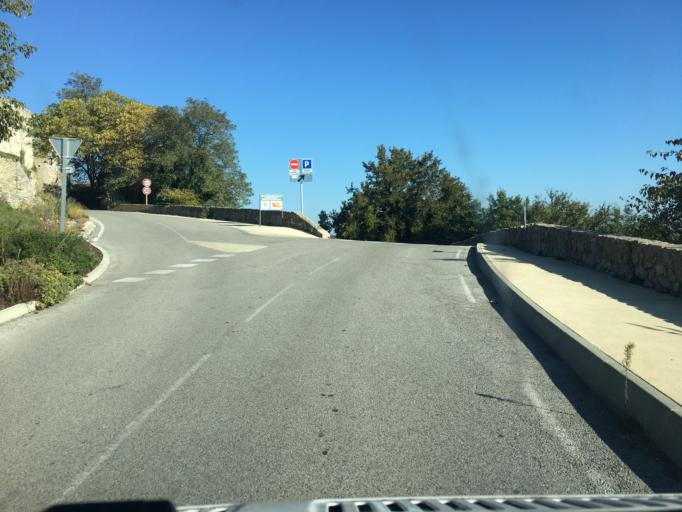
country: FR
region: Languedoc-Roussillon
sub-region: Departement du Gard
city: Goudargues
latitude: 44.1527
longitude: 4.3675
